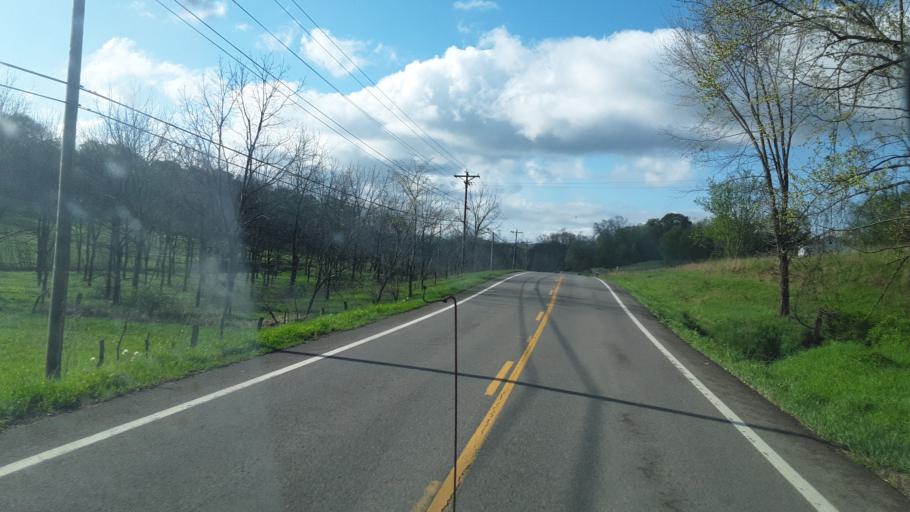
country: US
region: Ohio
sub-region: Muskingum County
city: New Concord
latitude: 39.9034
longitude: -81.6759
